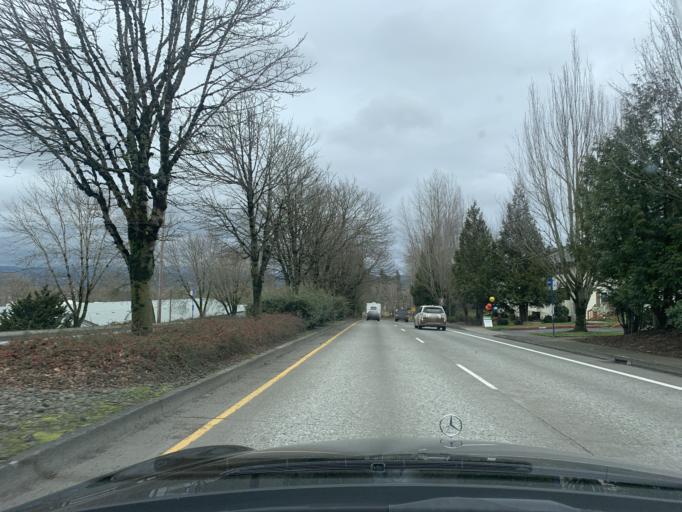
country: US
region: Oregon
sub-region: Multnomah County
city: Troutdale
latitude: 45.5380
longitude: -122.3931
